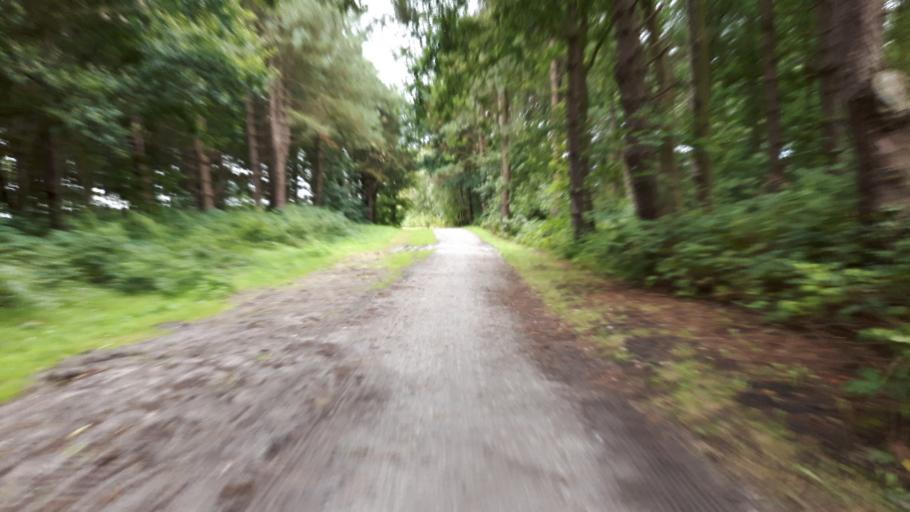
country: NL
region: Friesland
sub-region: Gemeente Ameland
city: Nes
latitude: 53.4517
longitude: 5.7137
